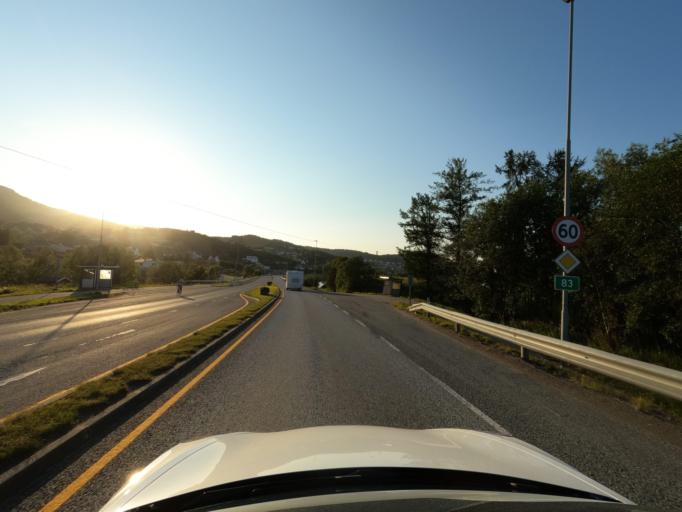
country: NO
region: Troms
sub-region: Harstad
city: Harstad
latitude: 68.7603
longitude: 16.5660
